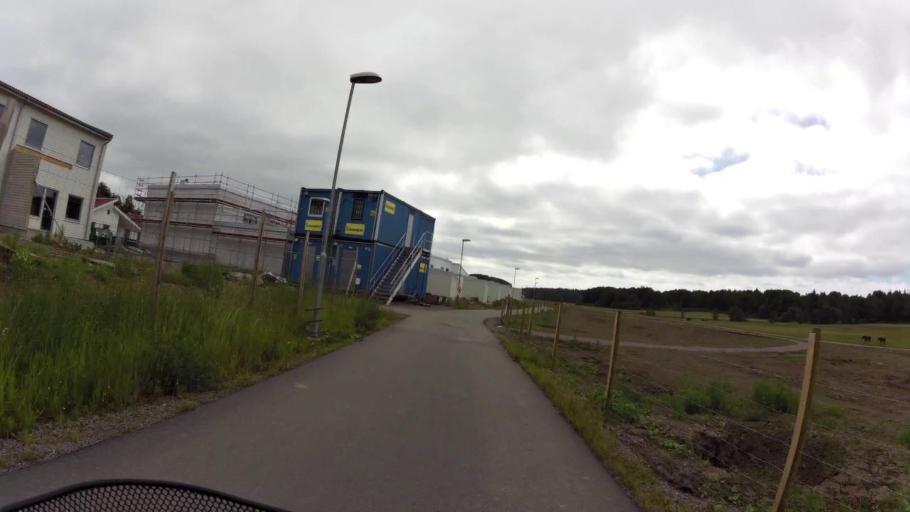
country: SE
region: OEstergoetland
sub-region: Linkopings Kommun
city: Sturefors
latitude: 58.3661
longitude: 15.6745
